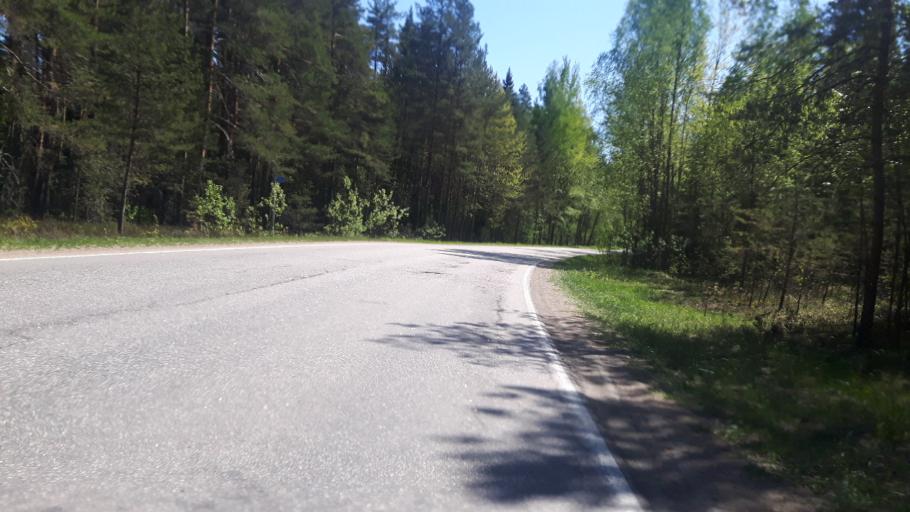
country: RU
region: Leningrad
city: Glebychevo
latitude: 60.3578
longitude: 28.8114
